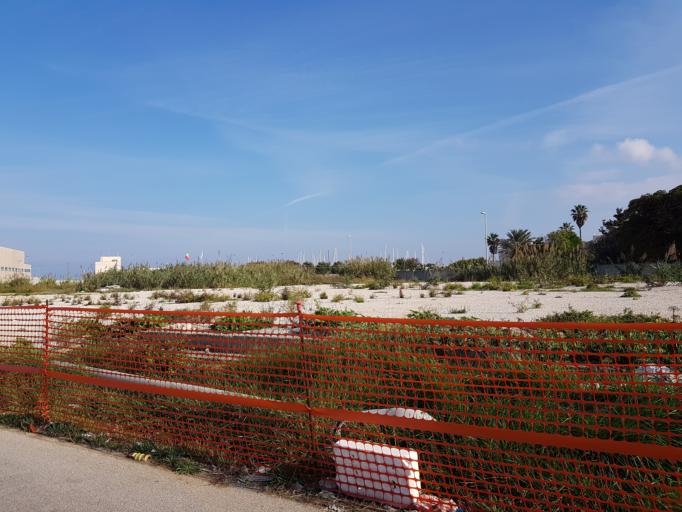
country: IT
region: Apulia
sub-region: Provincia di Brindisi
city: Materdomini
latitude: 40.6602
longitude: 17.9590
